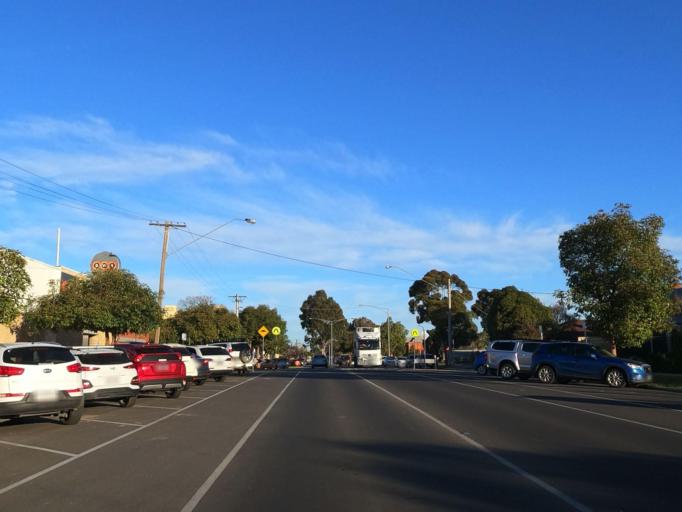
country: AU
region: Victoria
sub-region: Swan Hill
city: Swan Hill
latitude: -35.3375
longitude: 143.5577
